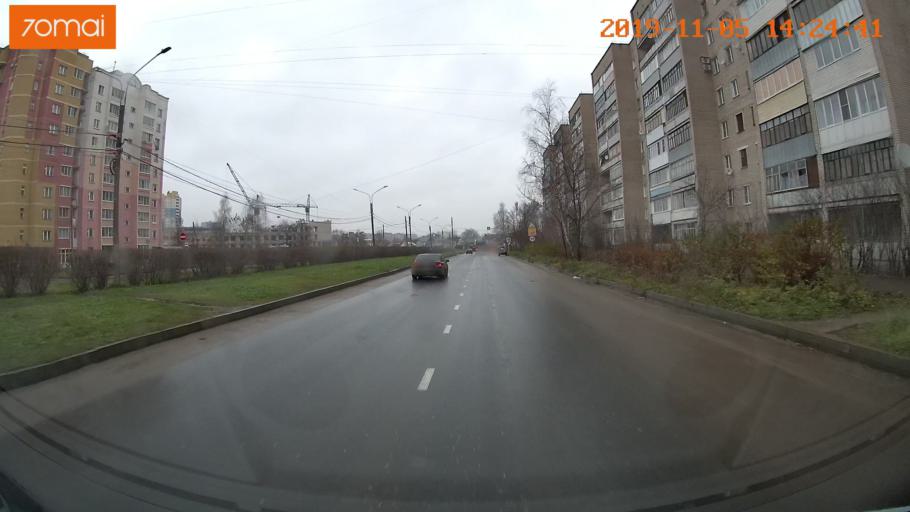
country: RU
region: Ivanovo
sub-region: Gorod Ivanovo
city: Ivanovo
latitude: 56.9695
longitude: 40.9960
